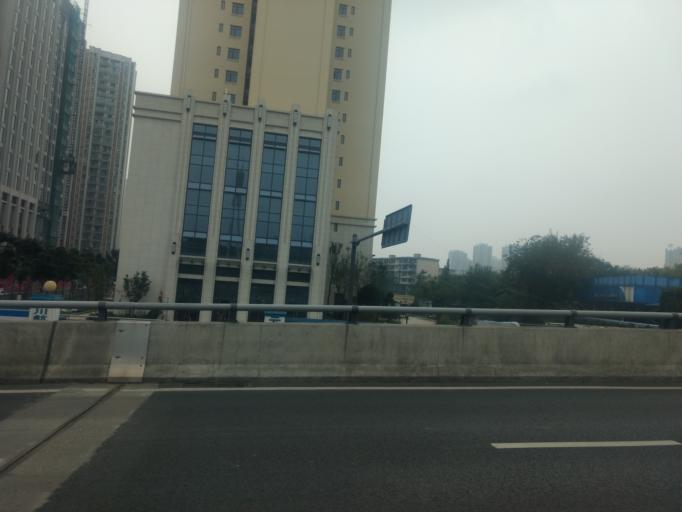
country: CN
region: Sichuan
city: Chengdu
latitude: 30.6834
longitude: 104.0959
